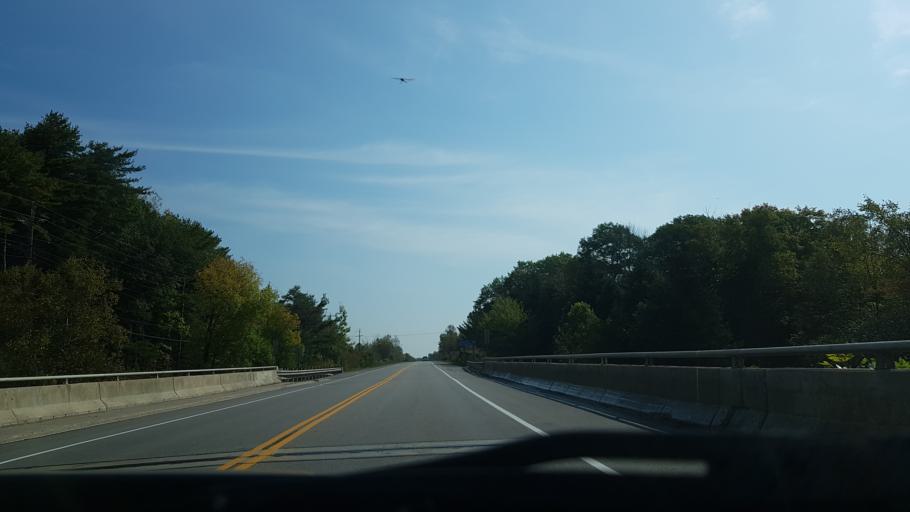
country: CA
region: Ontario
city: Orillia
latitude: 44.7436
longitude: -79.3146
